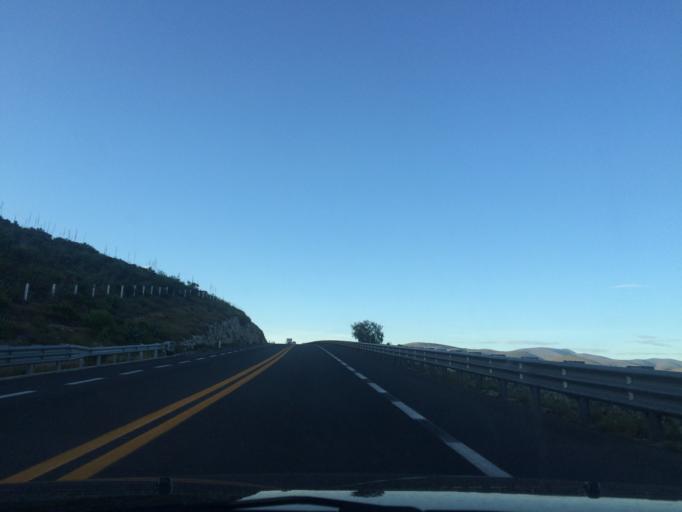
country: MX
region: Puebla
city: Cuacnopalan
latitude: 18.7866
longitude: -97.4887
